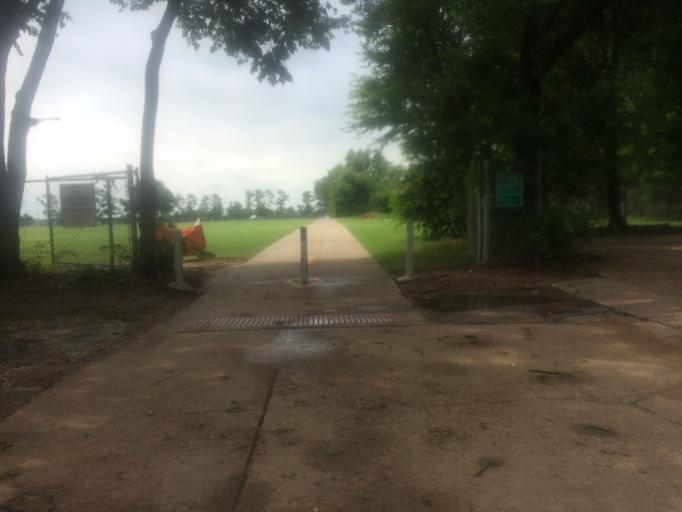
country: US
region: Oklahoma
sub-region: Cleveland County
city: Norman
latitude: 35.1997
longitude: -97.4402
